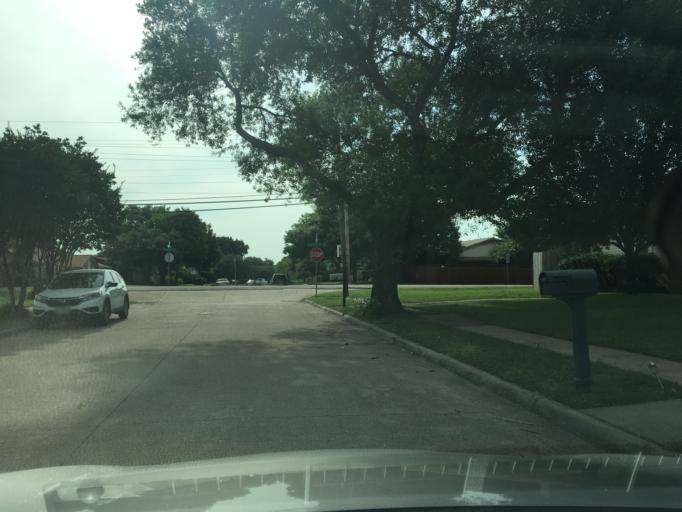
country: US
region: Texas
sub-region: Dallas County
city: Garland
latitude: 32.9626
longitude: -96.6704
